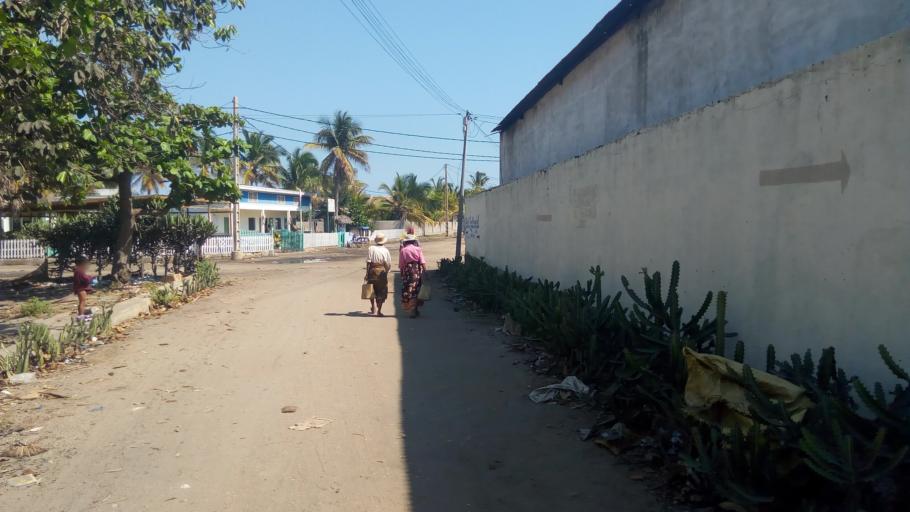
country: MG
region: Menabe
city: Morondava
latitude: -20.2948
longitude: 44.2788
